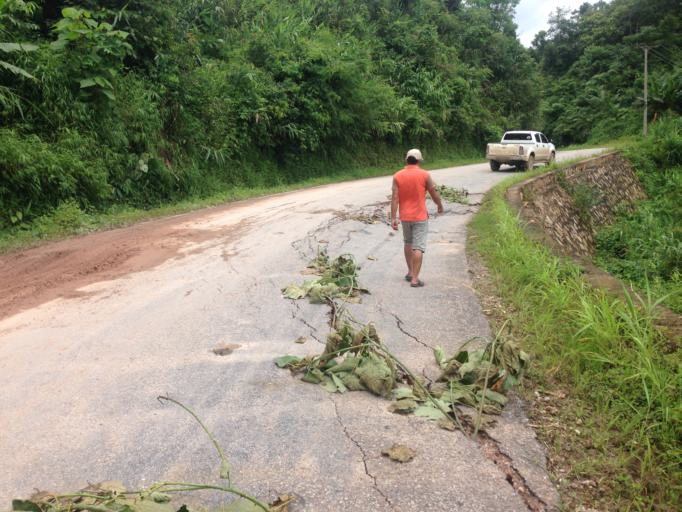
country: LA
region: Oudomxai
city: Muang La
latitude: 21.2357
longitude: 102.0701
